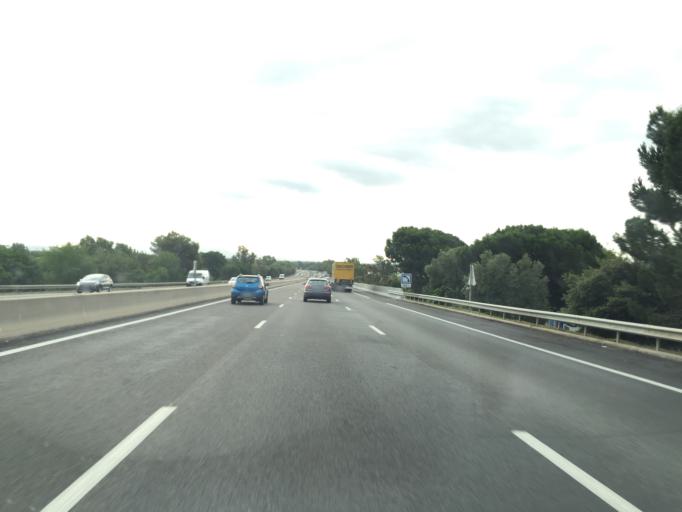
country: FR
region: Provence-Alpes-Cote d'Azur
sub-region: Departement du Var
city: Roquebrune-sur-Argens
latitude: 43.4642
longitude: 6.6285
